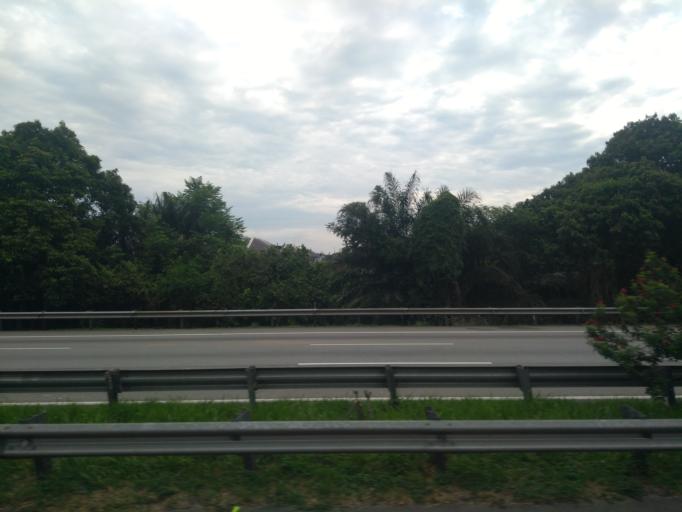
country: MY
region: Melaka
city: Alor Gajah
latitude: 2.3853
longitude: 102.2292
